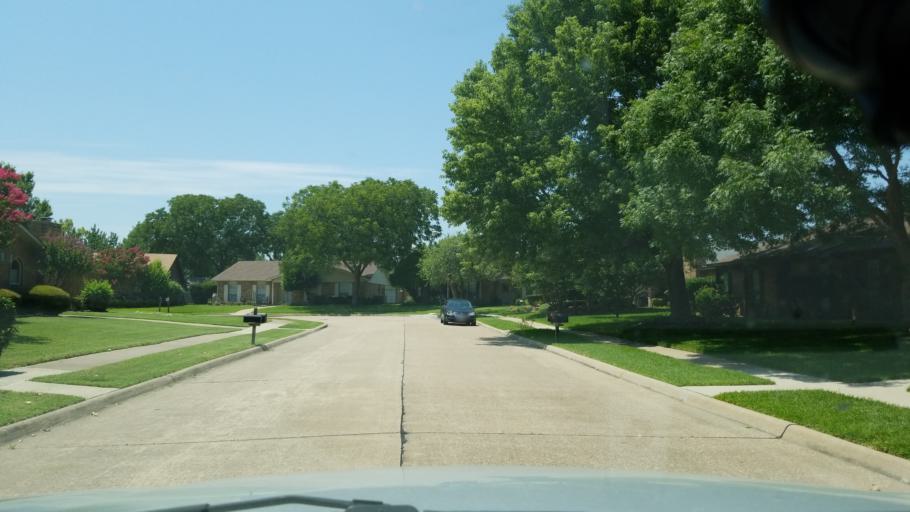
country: US
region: Texas
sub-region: Dallas County
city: Coppell
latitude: 32.9632
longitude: -96.9859
